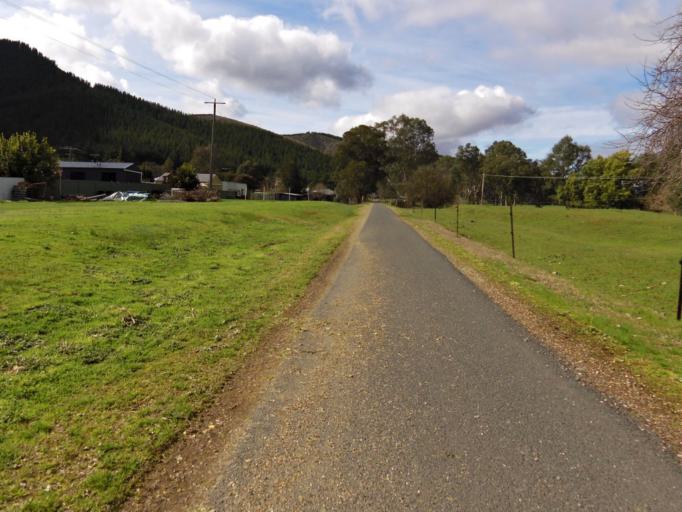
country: AU
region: Victoria
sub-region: Alpine
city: Mount Beauty
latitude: -36.5741
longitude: 146.7420
